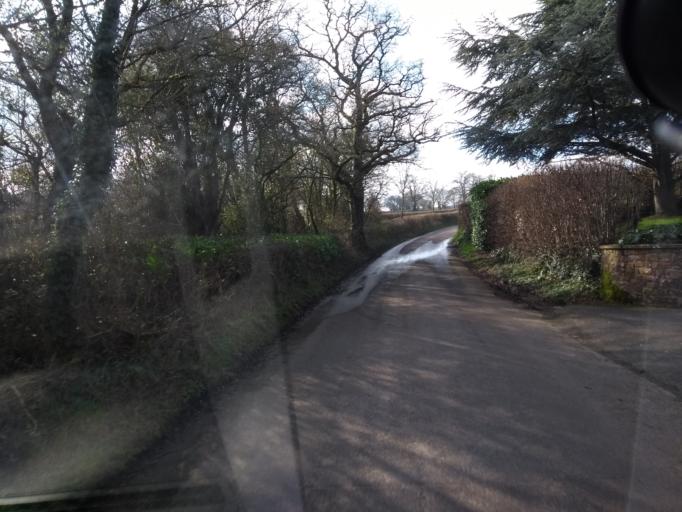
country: GB
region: England
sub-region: Somerset
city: Creech Saint Michael
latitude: 50.9529
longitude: -3.0336
